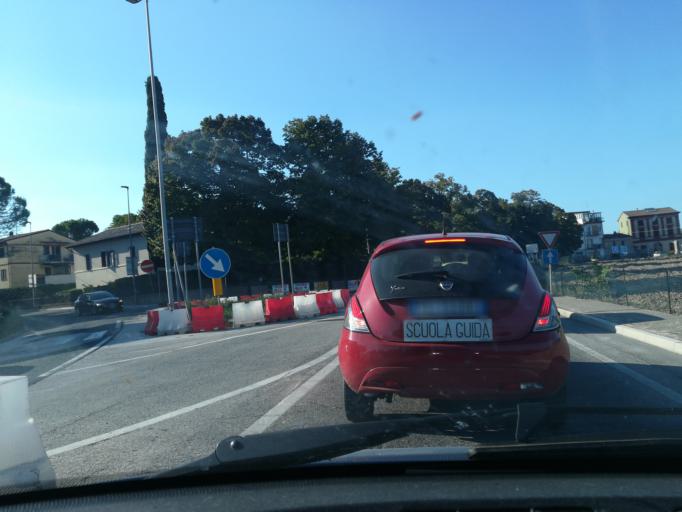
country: IT
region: The Marches
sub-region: Provincia di Macerata
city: Villa Potenza
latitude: 43.3283
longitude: 13.4249
